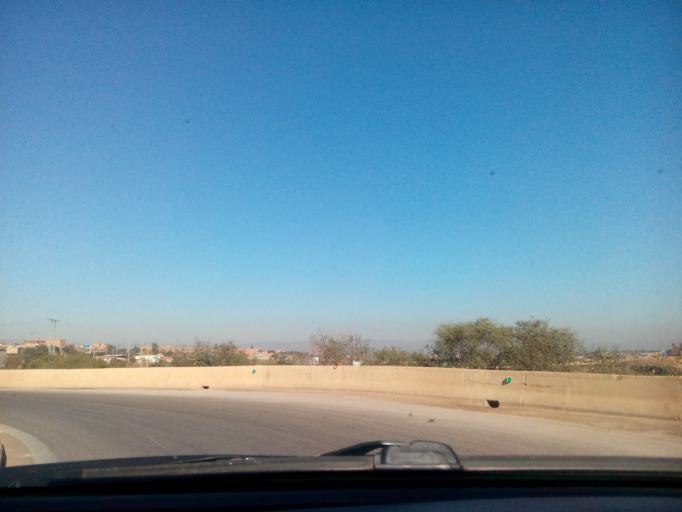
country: DZ
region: Chlef
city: Boukadir
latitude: 36.0550
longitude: 1.1455
